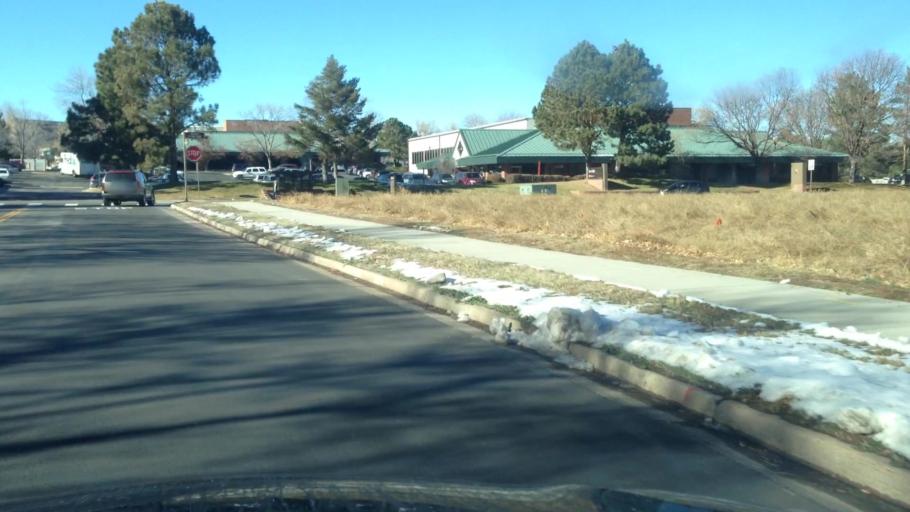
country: US
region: Colorado
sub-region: Douglas County
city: Meridian
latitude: 39.5670
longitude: -104.8612
